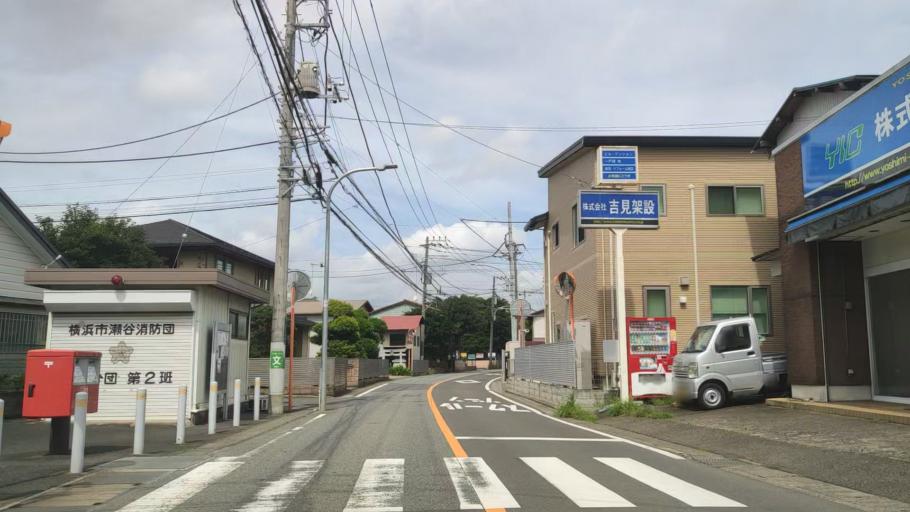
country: JP
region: Kanagawa
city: Minami-rinkan
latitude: 35.4896
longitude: 139.4731
